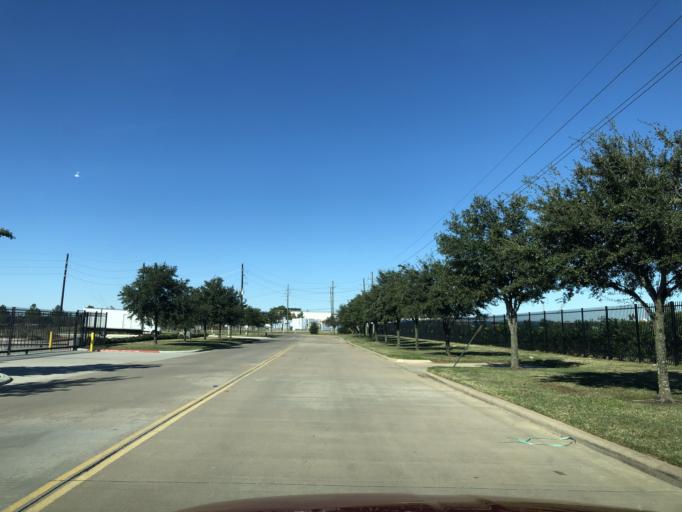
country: US
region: Texas
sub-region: Harris County
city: Oak Cliff Place
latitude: 29.9356
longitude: -95.6536
